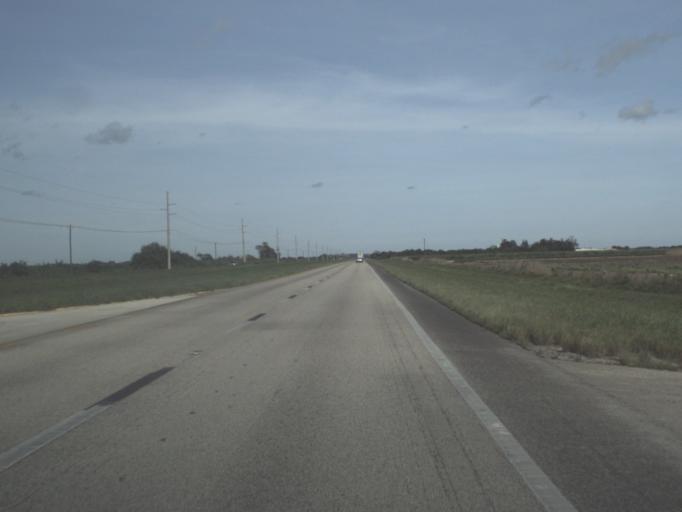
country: US
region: Florida
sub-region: Glades County
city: Moore Haven
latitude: 26.7886
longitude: -81.0826
